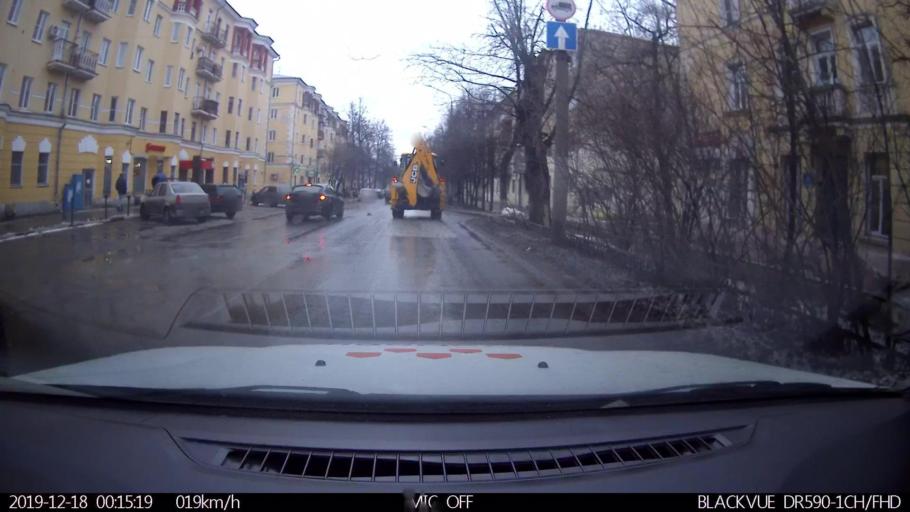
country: RU
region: Nizjnij Novgorod
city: Nizhniy Novgorod
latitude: 56.3329
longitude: 43.8804
